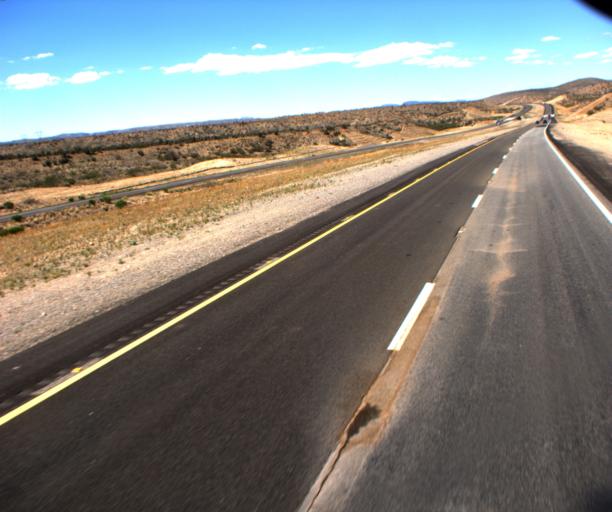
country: US
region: Arizona
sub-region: Mohave County
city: Kingman
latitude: 34.9850
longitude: -113.6672
